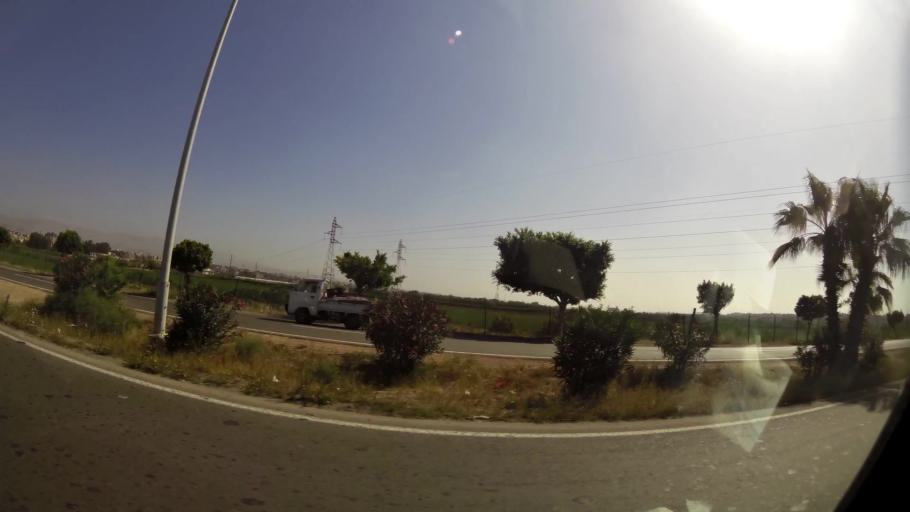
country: MA
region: Souss-Massa-Draa
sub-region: Inezgane-Ait Mellou
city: Inezgane
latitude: 30.3641
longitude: -9.4941
